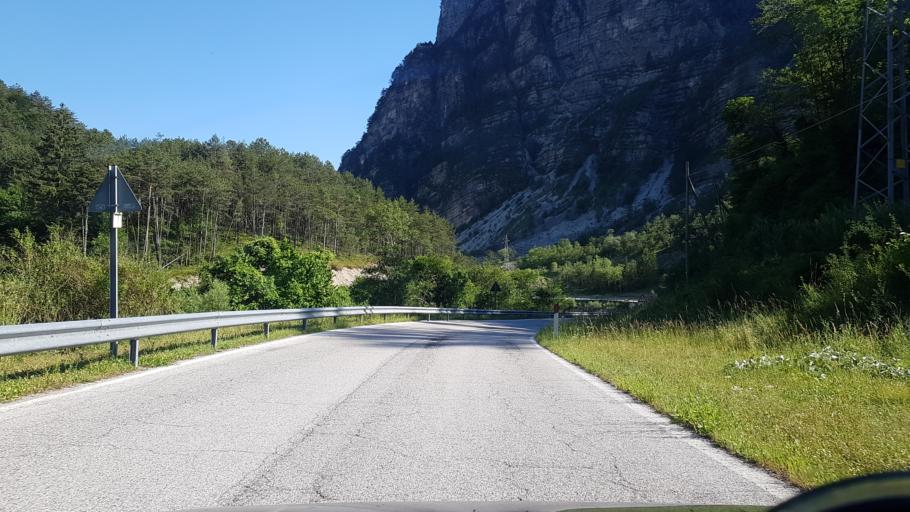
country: IT
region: Friuli Venezia Giulia
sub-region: Provincia di Udine
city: Moggio Udinese
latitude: 46.4496
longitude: 13.1878
